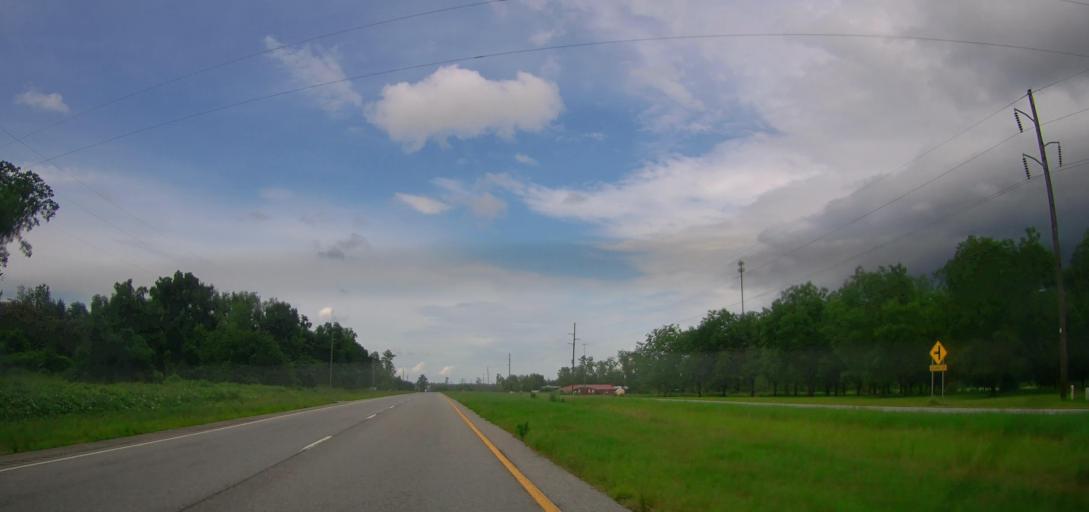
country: US
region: Georgia
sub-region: Pierce County
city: Blackshear
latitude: 31.4289
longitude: -82.0928
